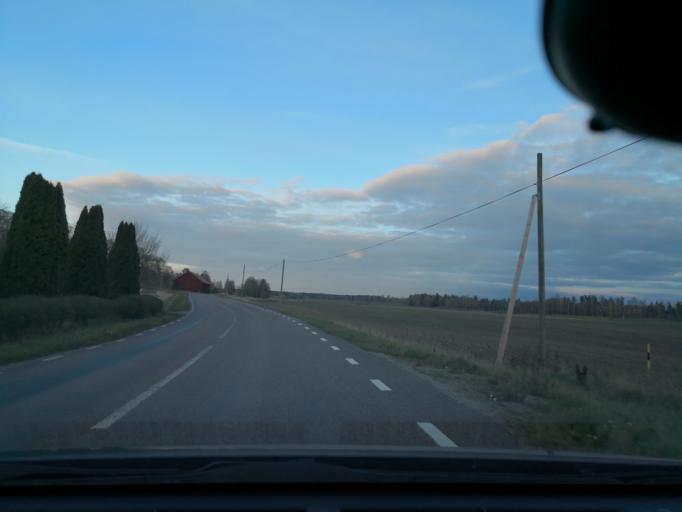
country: SE
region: Vaestmanland
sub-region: Vasteras
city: Tillberga
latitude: 59.6360
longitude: 16.6696
